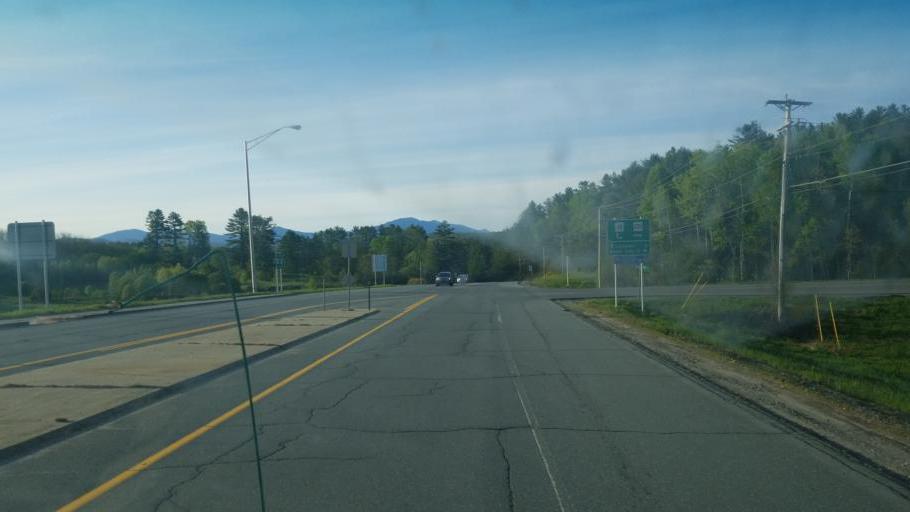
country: US
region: New Hampshire
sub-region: Grafton County
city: Littleton
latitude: 44.3240
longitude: -71.8053
